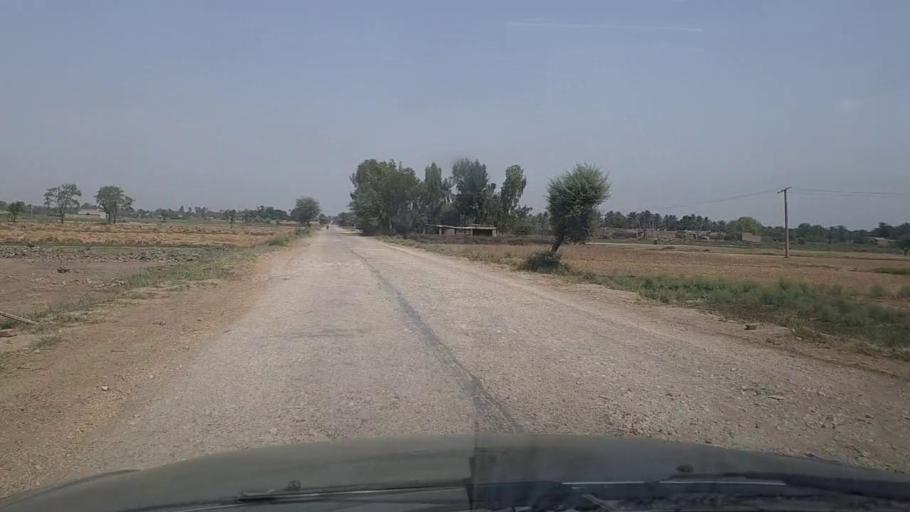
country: PK
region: Sindh
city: Setharja Old
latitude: 27.1592
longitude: 68.5195
